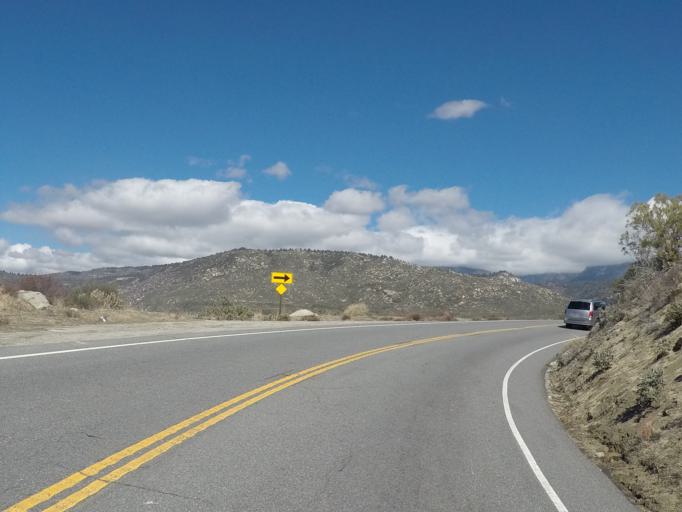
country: US
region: California
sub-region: Riverside County
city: Idyllwild-Pine Cove
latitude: 33.6979
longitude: -116.7569
